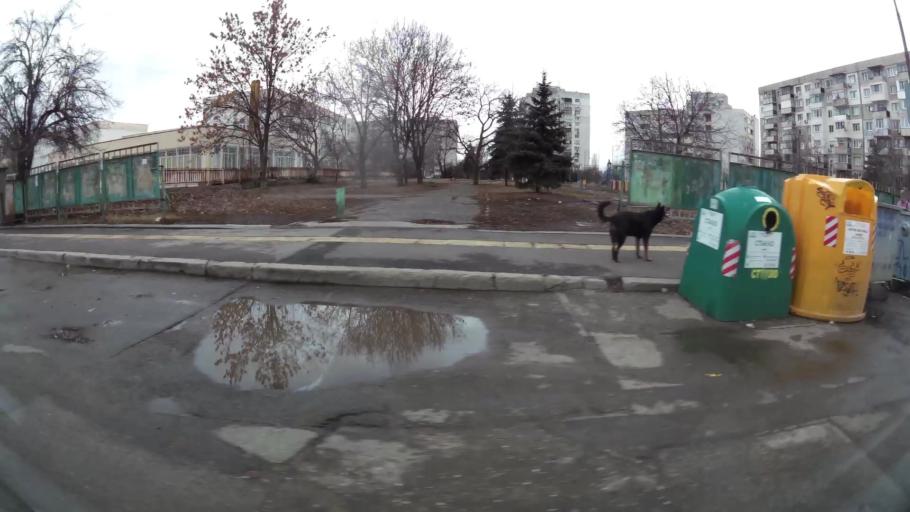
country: BG
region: Sofia-Capital
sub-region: Stolichna Obshtina
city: Sofia
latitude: 42.7369
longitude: 23.2883
